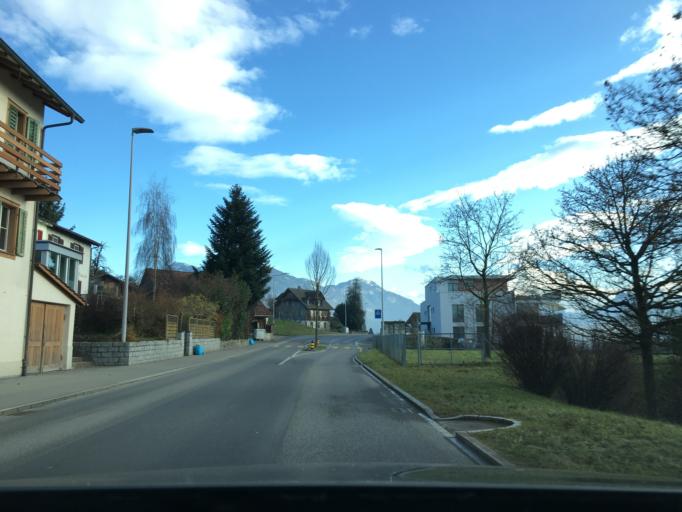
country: CH
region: Lucerne
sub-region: Lucerne-Land District
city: Meggen
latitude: 47.0507
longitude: 8.3606
